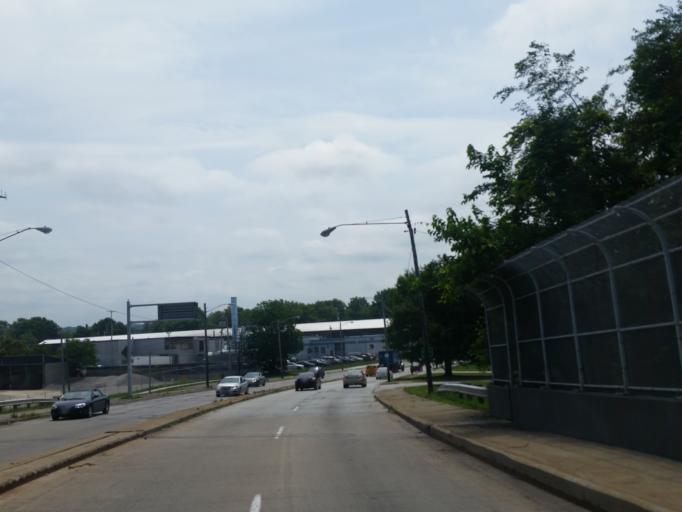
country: US
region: Ohio
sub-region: Cuyahoga County
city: Bratenahl
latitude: 41.5500
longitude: -81.6023
